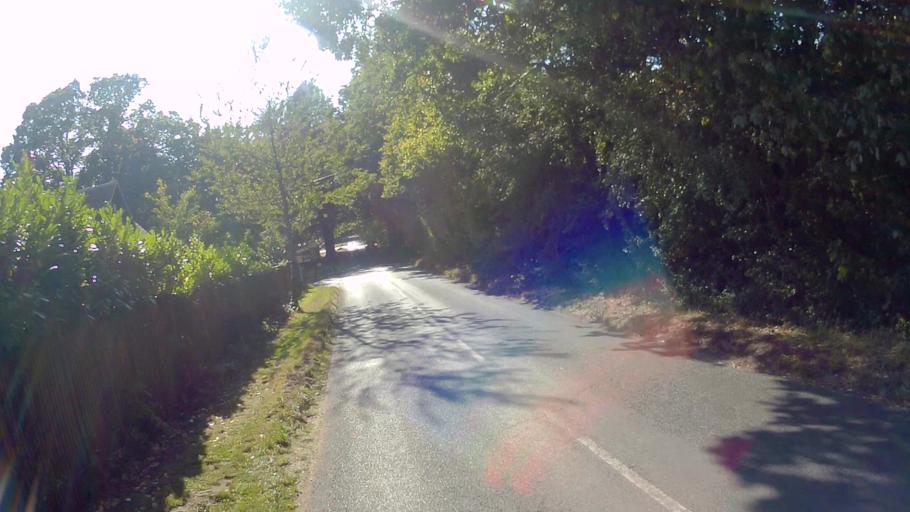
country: GB
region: England
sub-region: Surrey
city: Farnham
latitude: 51.1802
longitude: -0.7767
